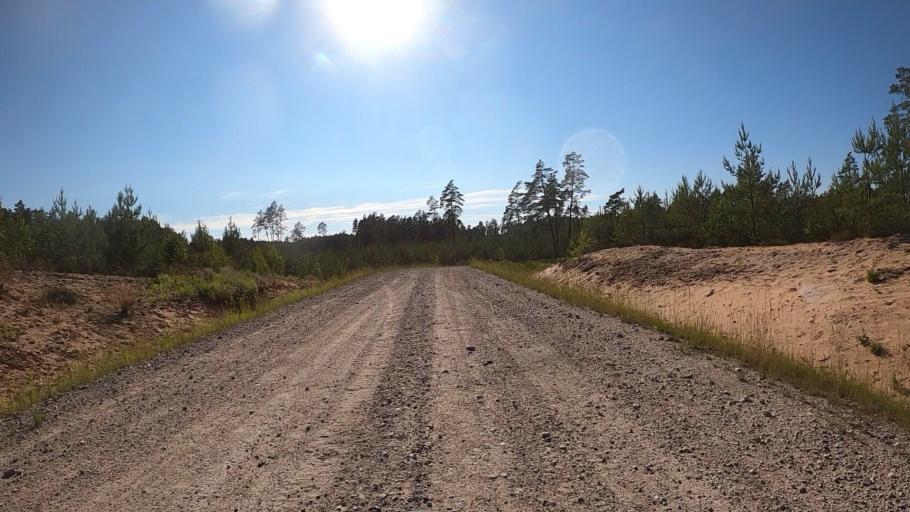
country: LV
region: Carnikava
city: Carnikava
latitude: 57.0948
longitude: 24.2437
